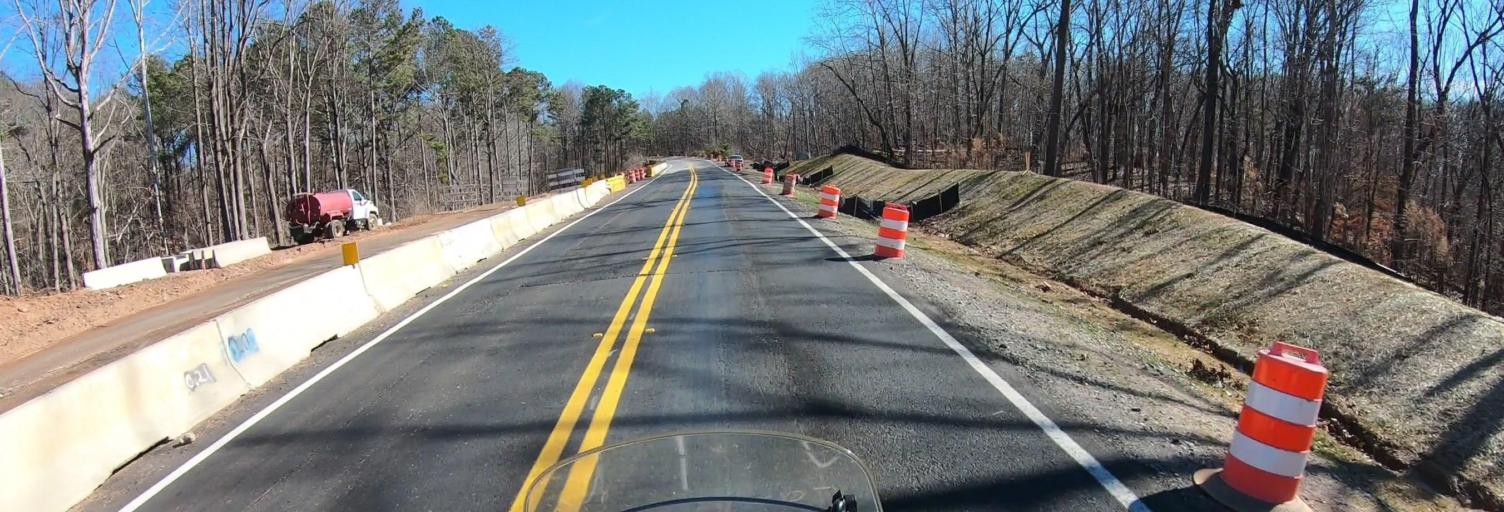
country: US
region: Georgia
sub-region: Hall County
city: Oakwood
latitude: 34.2601
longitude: -83.9467
